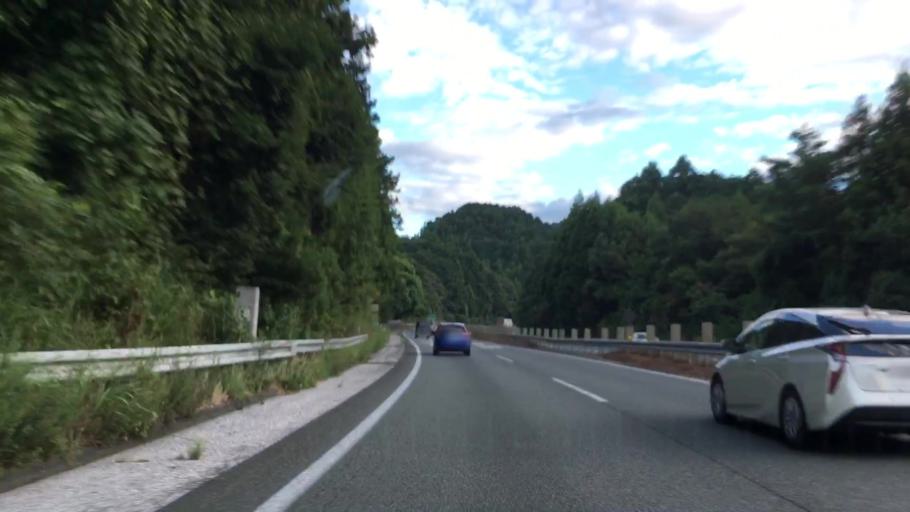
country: JP
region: Yamaguchi
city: Ogori-shimogo
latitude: 34.1661
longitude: 131.2410
